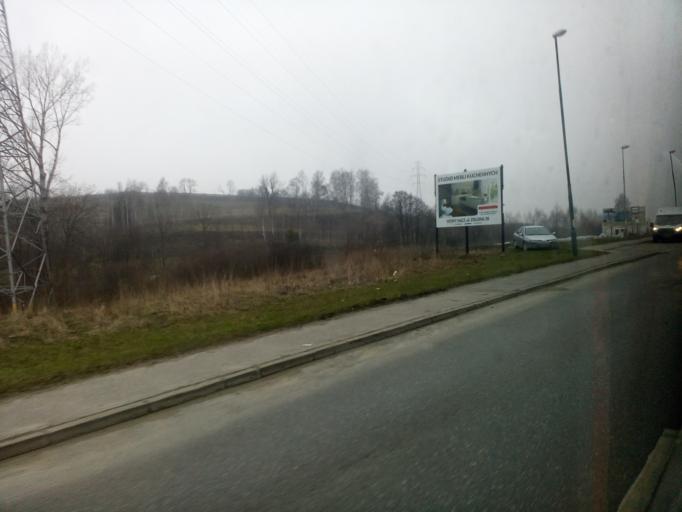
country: PL
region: Lesser Poland Voivodeship
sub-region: Powiat nowosadecki
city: Stary Sacz
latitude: 49.5755
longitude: 20.6635
